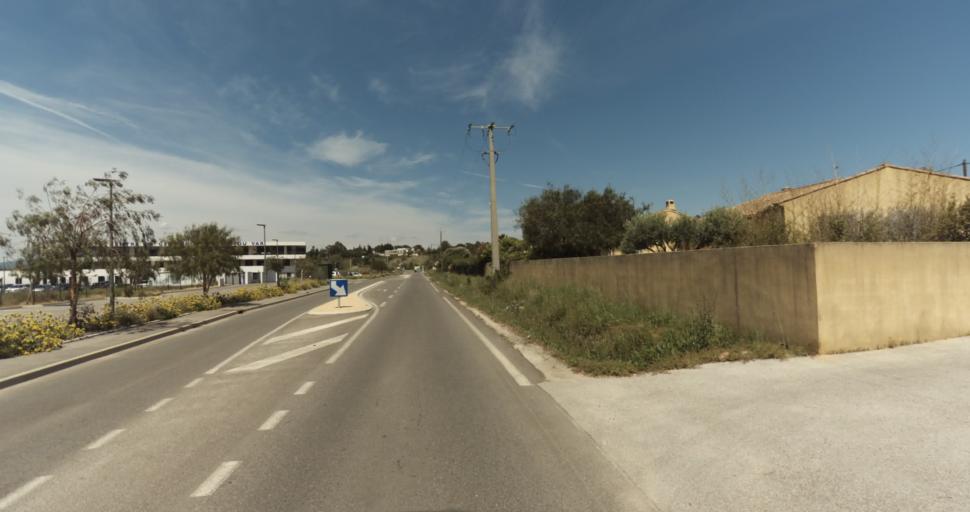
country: FR
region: Provence-Alpes-Cote d'Azur
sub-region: Departement du Var
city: La Crau
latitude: 43.1304
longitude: 6.0770
